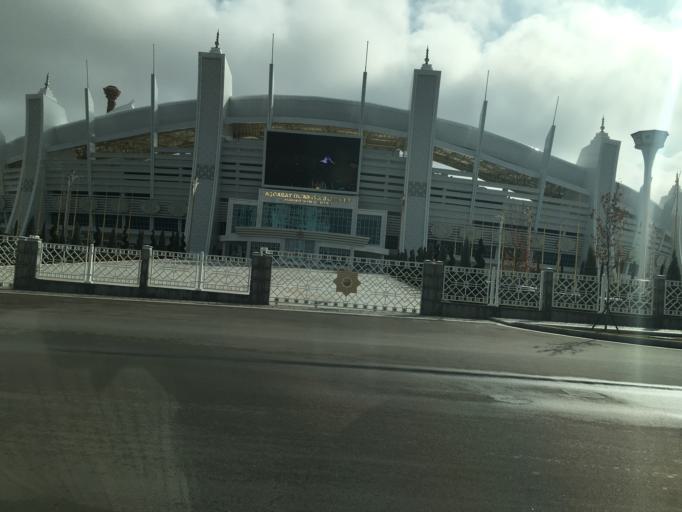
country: TM
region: Ahal
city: Ashgabat
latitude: 37.9052
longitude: 58.3742
